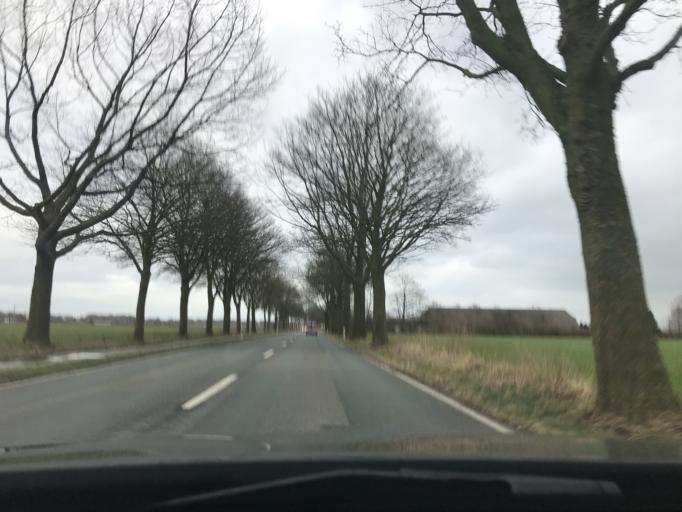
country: DE
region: North Rhine-Westphalia
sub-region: Regierungsbezirk Dusseldorf
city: Uedem
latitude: 51.6913
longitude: 6.2499
